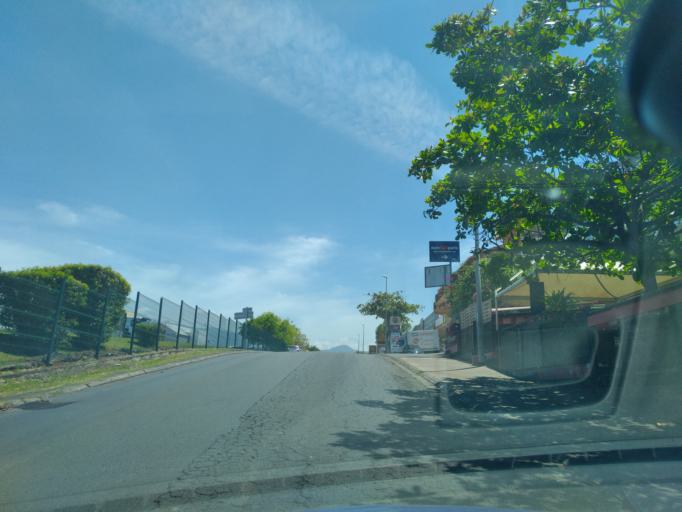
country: RE
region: Reunion
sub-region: Reunion
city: Saint-Pierre
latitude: -21.3220
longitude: 55.4488
